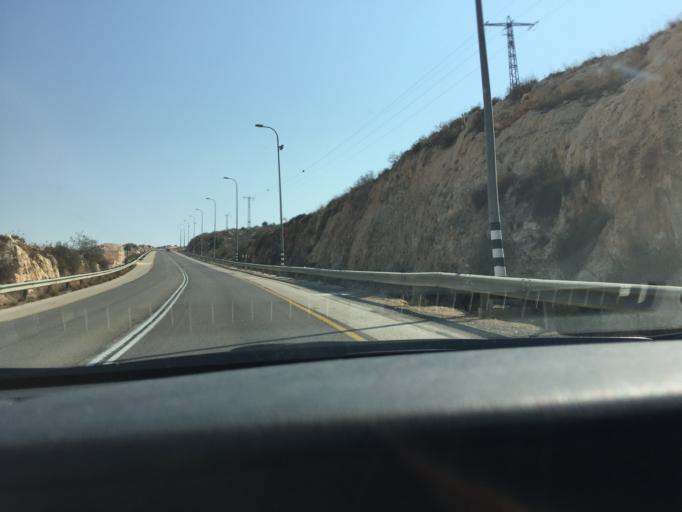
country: PS
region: West Bank
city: Bruqin
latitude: 32.0894
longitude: 35.1031
